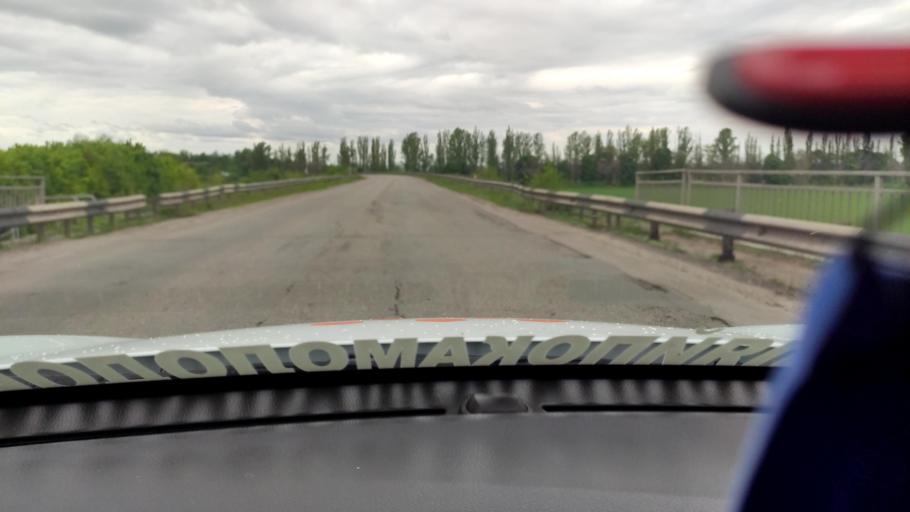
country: RU
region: Voronezj
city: Liski
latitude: 51.0125
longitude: 39.5573
